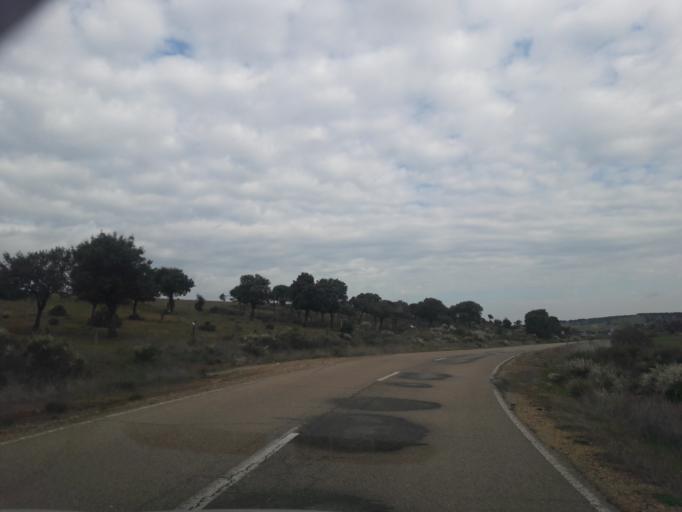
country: ES
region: Castille and Leon
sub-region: Provincia de Salamanca
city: Pastores
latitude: 40.5333
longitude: -6.5258
